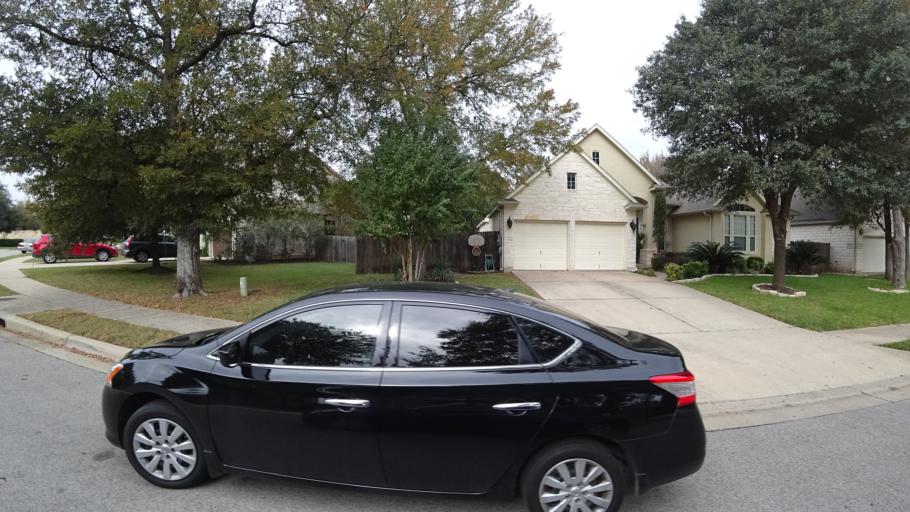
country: US
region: Texas
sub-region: Travis County
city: Shady Hollow
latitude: 30.1981
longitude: -97.8995
